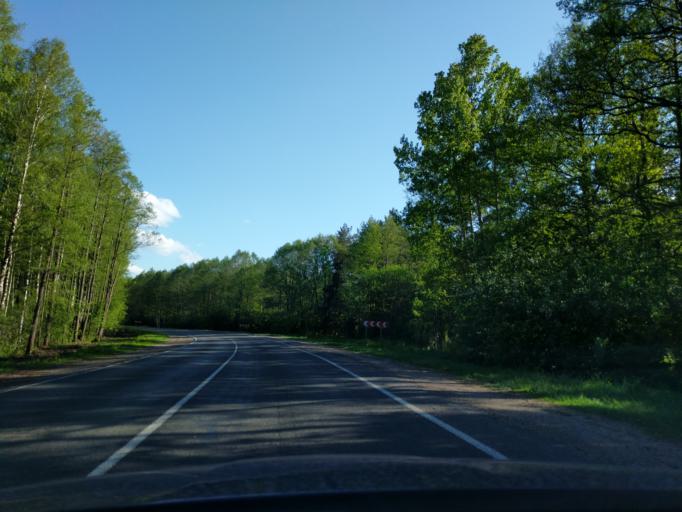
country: BY
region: Minsk
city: Myadzyel
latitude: 54.8443
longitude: 26.9259
